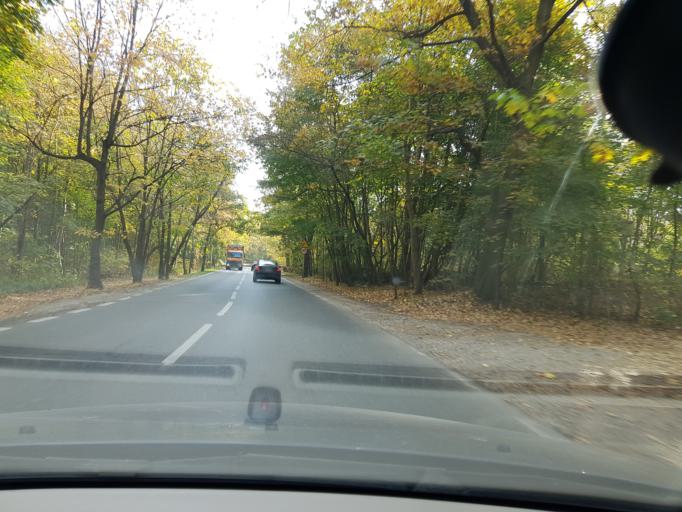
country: PL
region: Masovian Voivodeship
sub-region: Warszawa
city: Bemowo
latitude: 52.2653
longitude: 20.8820
